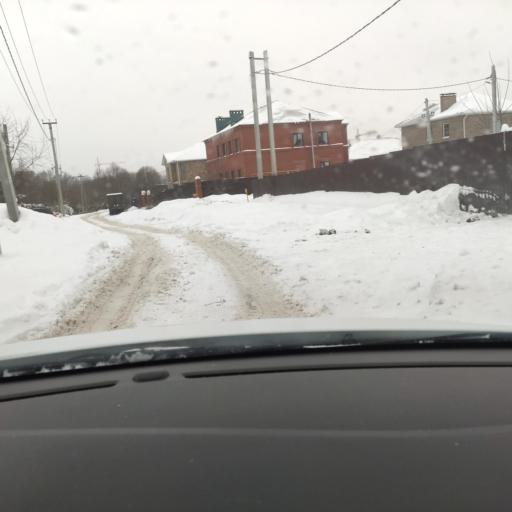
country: RU
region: Tatarstan
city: Vysokaya Gora
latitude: 55.8014
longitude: 49.2525
